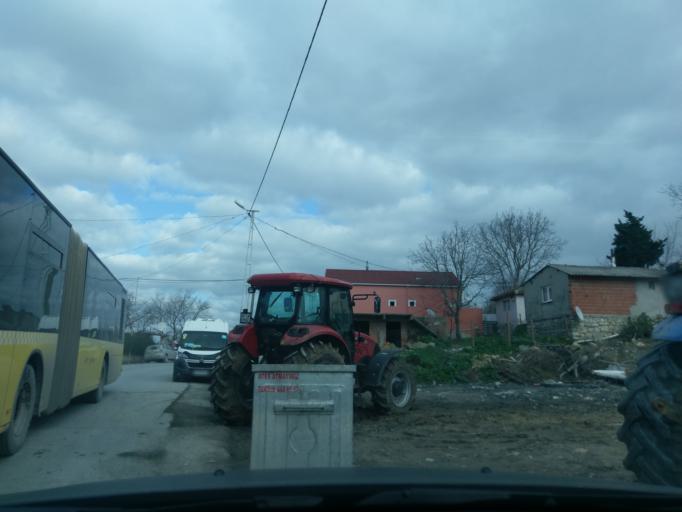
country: TR
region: Istanbul
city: Durusu
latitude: 41.2710
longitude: 28.6912
